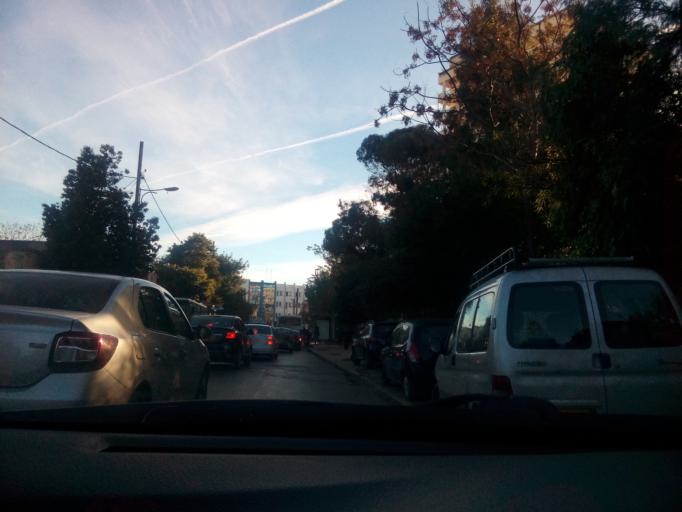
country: DZ
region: Oran
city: Oran
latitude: 35.6861
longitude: -0.6493
